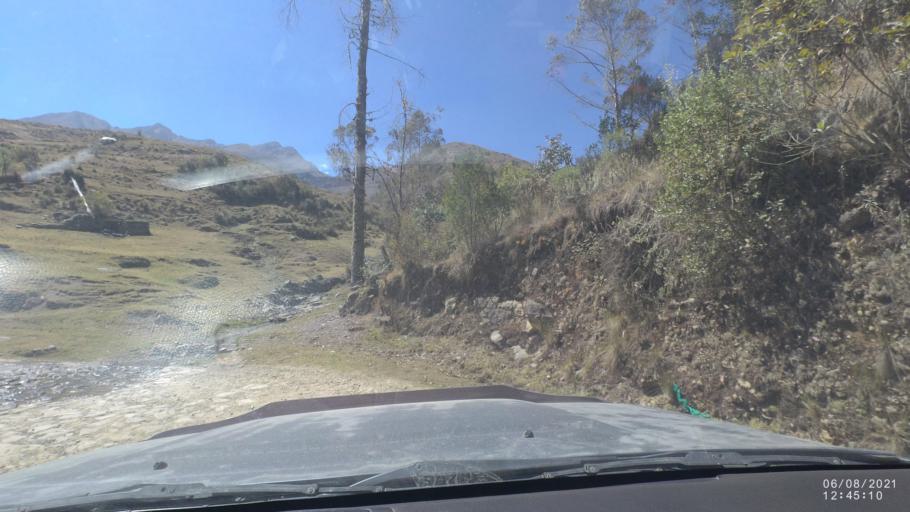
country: BO
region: Cochabamba
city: Colchani
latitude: -16.7662
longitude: -66.6637
